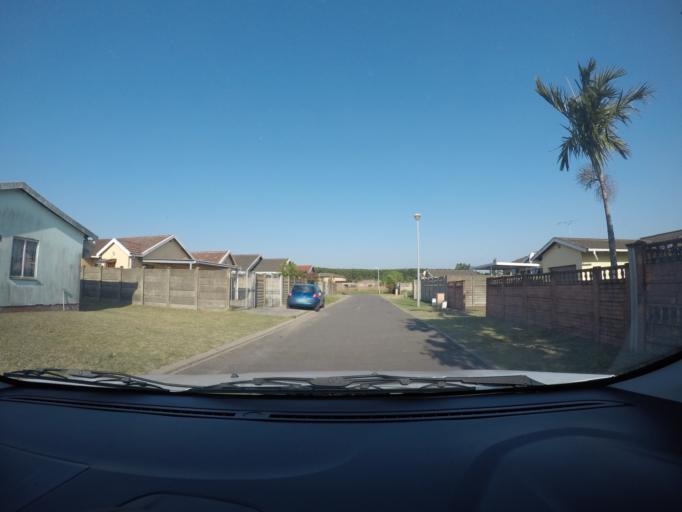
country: ZA
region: KwaZulu-Natal
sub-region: uThungulu District Municipality
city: Richards Bay
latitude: -28.7126
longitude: 32.0382
